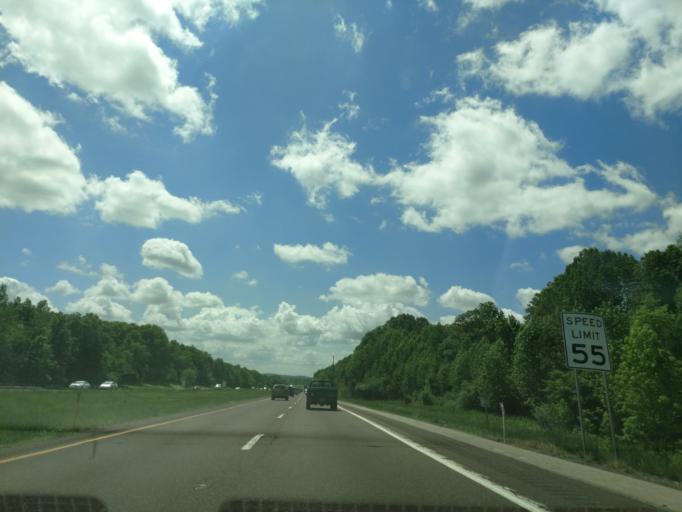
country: US
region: Pennsylvania
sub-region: Montgomery County
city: Audubon
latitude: 40.1164
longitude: -75.4287
